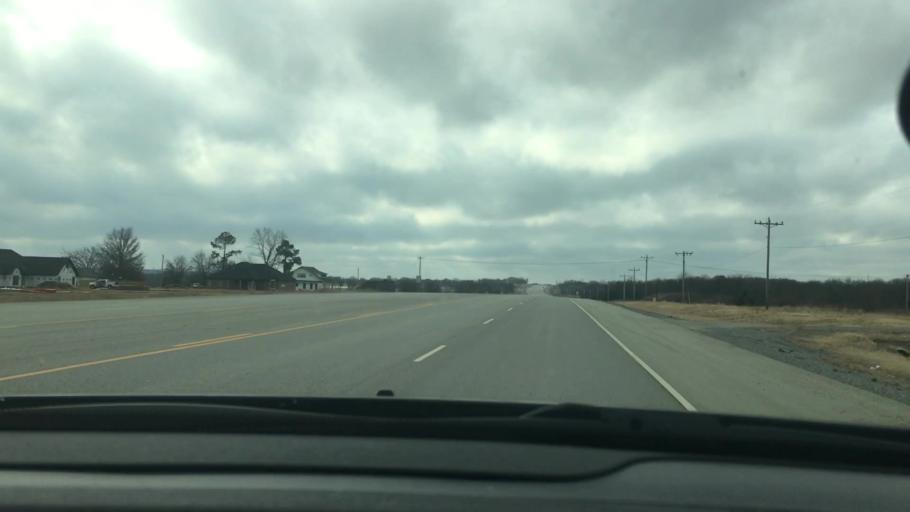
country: US
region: Oklahoma
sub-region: Bryan County
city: Durant
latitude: 34.0724
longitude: -96.3731
